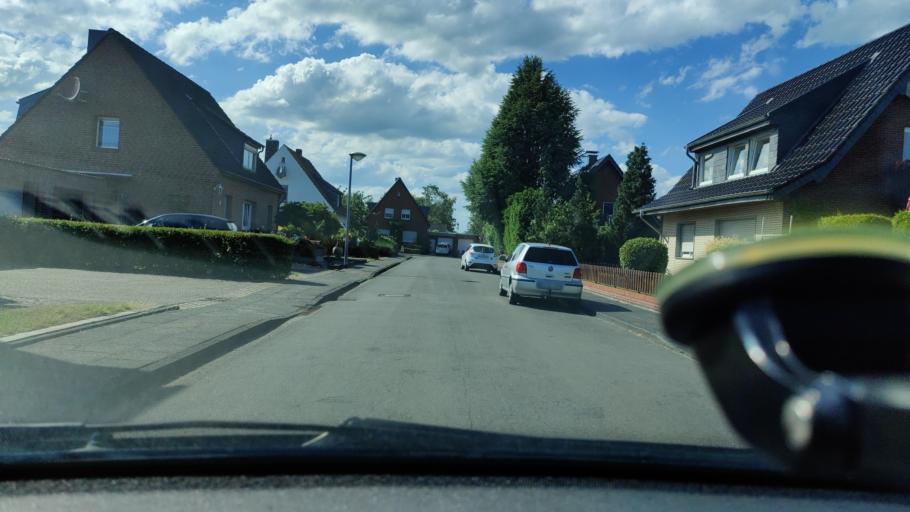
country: DE
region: North Rhine-Westphalia
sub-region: Regierungsbezirk Dusseldorf
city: Alpen
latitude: 51.5580
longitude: 6.5524
